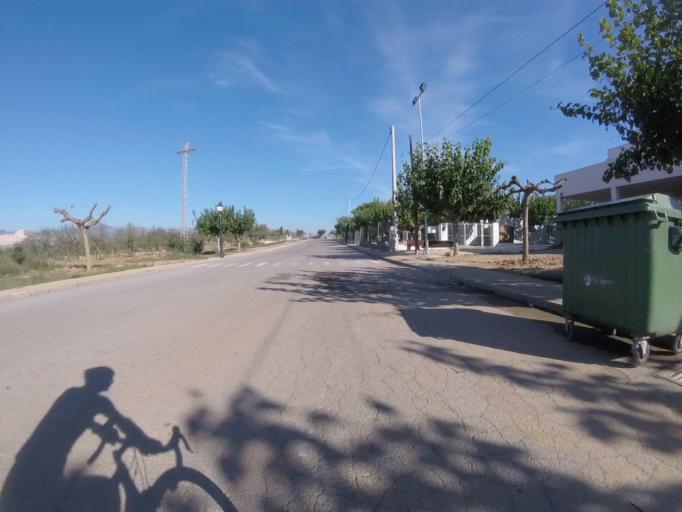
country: ES
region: Valencia
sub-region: Provincia de Castello
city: Benlloch
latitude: 40.2329
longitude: 0.0767
